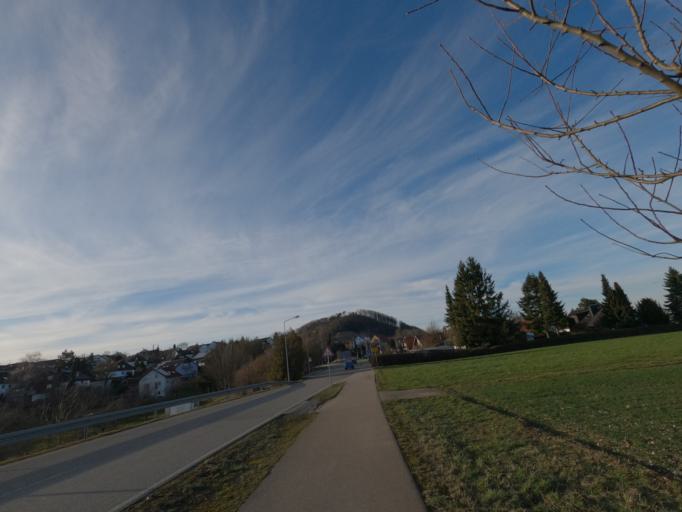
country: DE
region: Baden-Wuerttemberg
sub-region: Regierungsbezirk Stuttgart
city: Waldstetten
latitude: 48.7481
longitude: 9.7985
